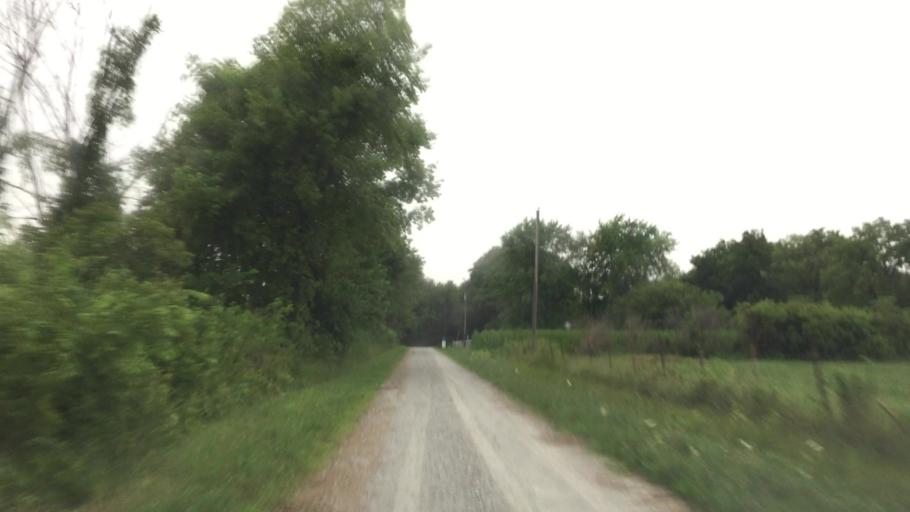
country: US
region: Iowa
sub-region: Lee County
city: Fort Madison
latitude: 40.6065
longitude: -91.2730
